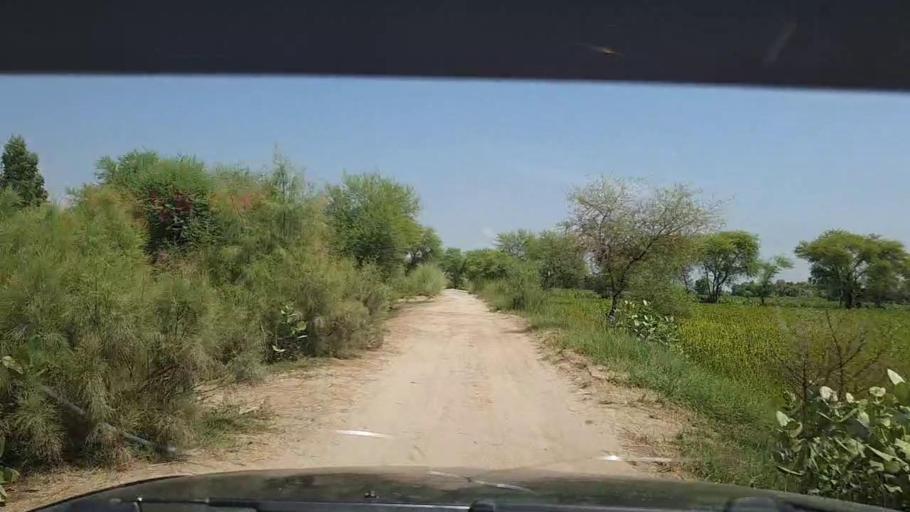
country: PK
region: Sindh
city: Tangwani
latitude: 28.2334
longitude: 68.9725
